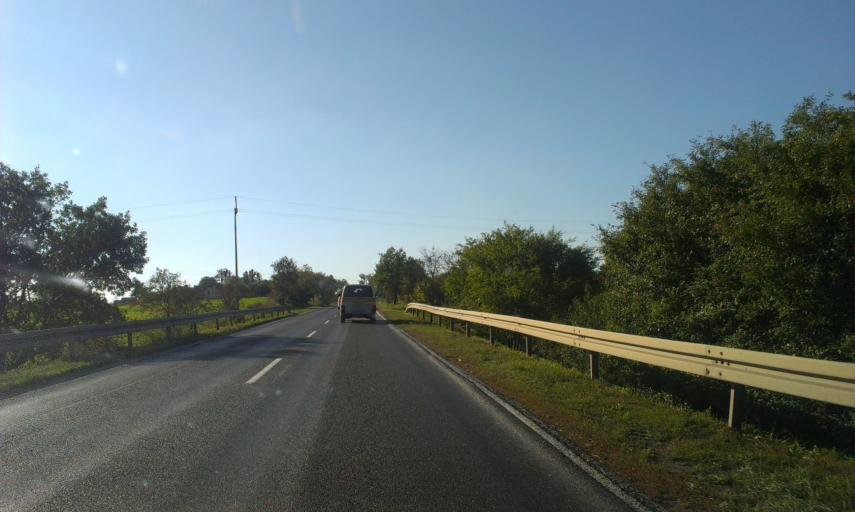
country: PL
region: Kujawsko-Pomorskie
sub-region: Powiat swiecki
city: Swiecie
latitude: 53.4180
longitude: 18.3531
